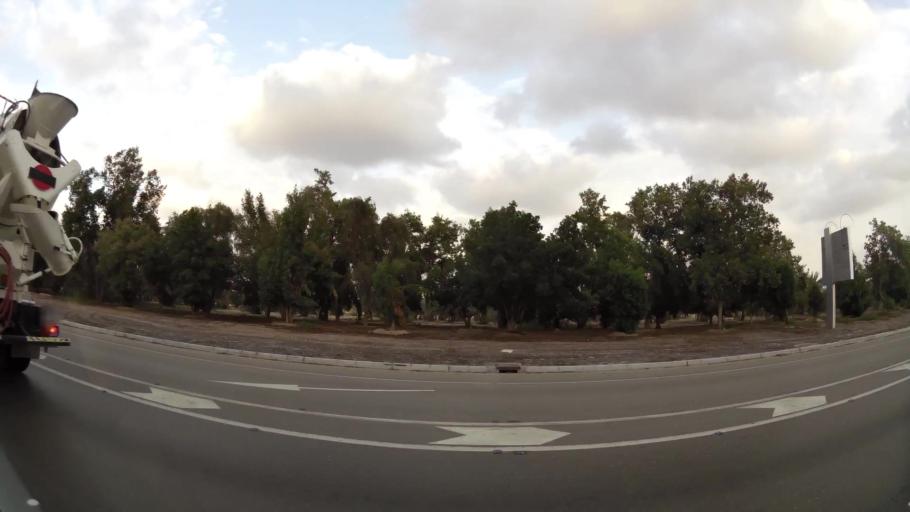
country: AE
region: Abu Dhabi
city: Abu Dhabi
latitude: 24.3991
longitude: 54.5237
